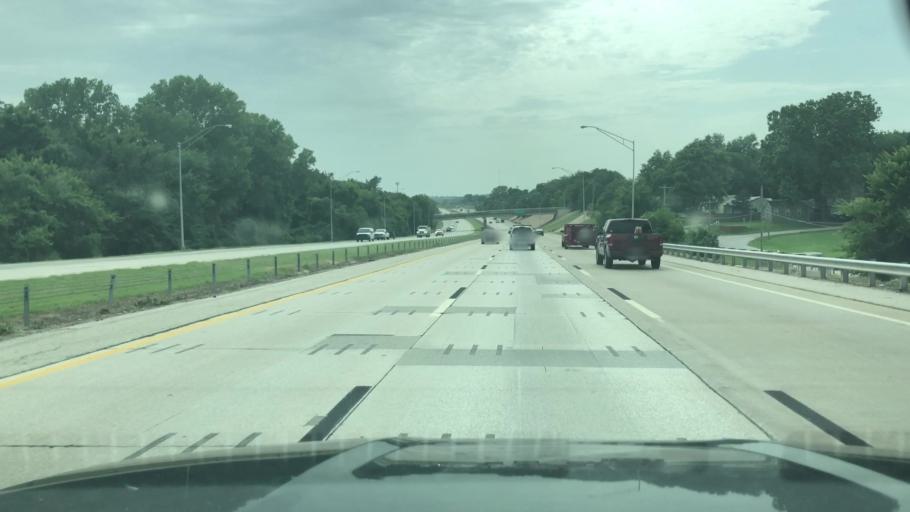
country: US
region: Oklahoma
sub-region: Tulsa County
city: Tulsa
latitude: 36.1584
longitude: -96.0342
